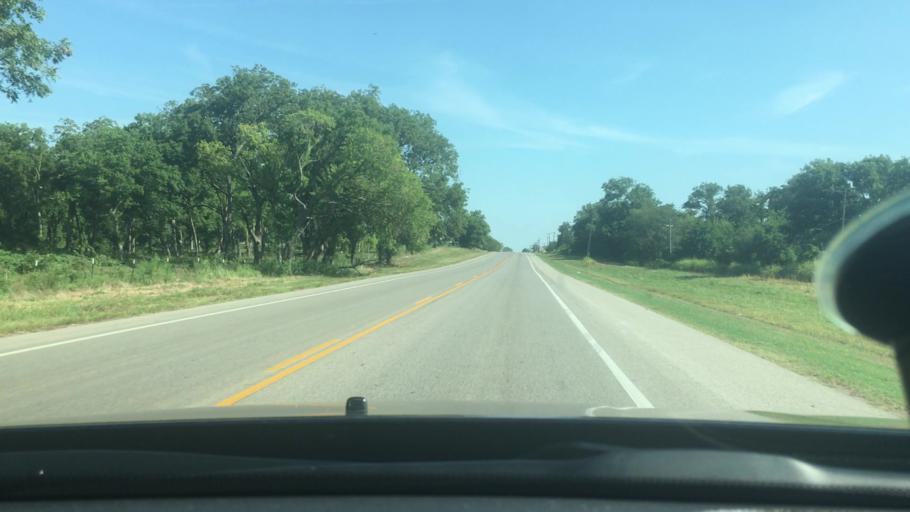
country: US
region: Oklahoma
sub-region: Garvin County
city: Pauls Valley
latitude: 34.6987
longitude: -97.2128
